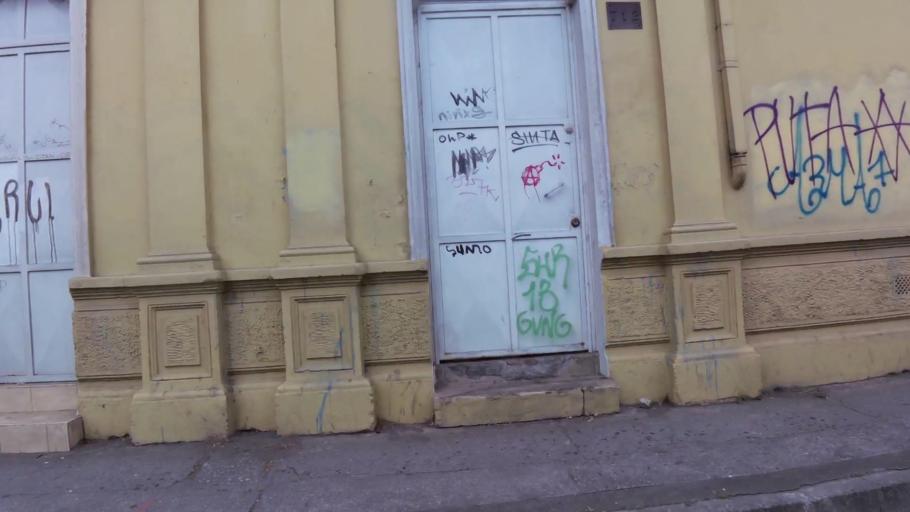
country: CL
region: Biobio
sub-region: Provincia de Concepcion
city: Concepcion
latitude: -36.8183
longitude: -73.0374
